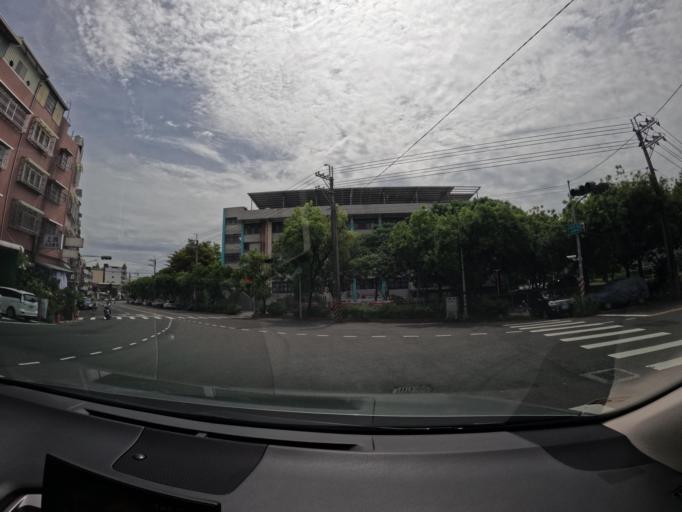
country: TW
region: Kaohsiung
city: Kaohsiung
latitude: 22.6886
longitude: 120.2921
